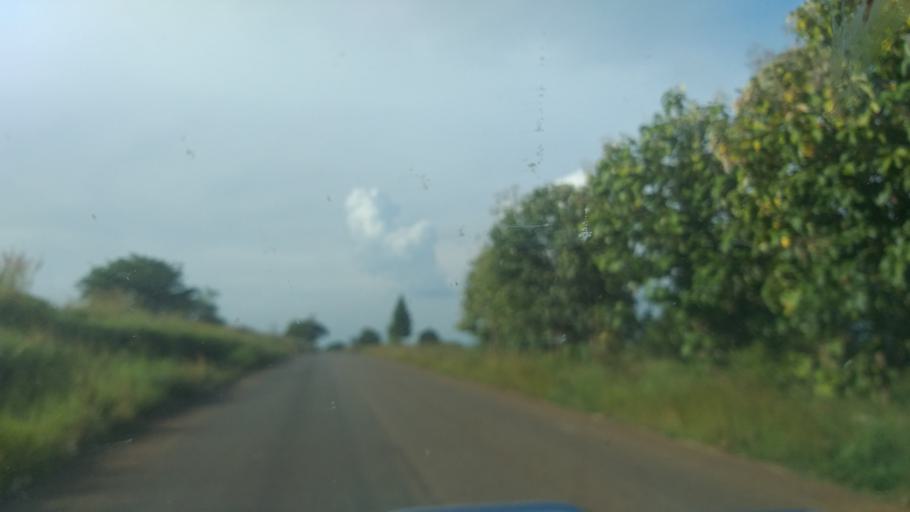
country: UG
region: Northern Region
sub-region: Arua District
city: Arua
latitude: 2.8379
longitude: 30.9926
